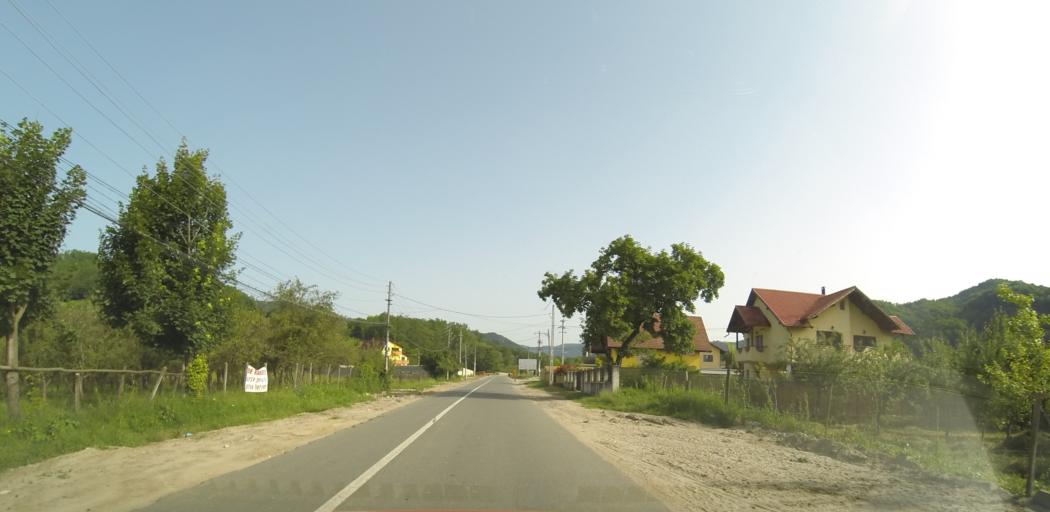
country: RO
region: Valcea
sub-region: Oras Baile Olanesti
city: Olanesti
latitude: 45.1732
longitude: 24.2578
